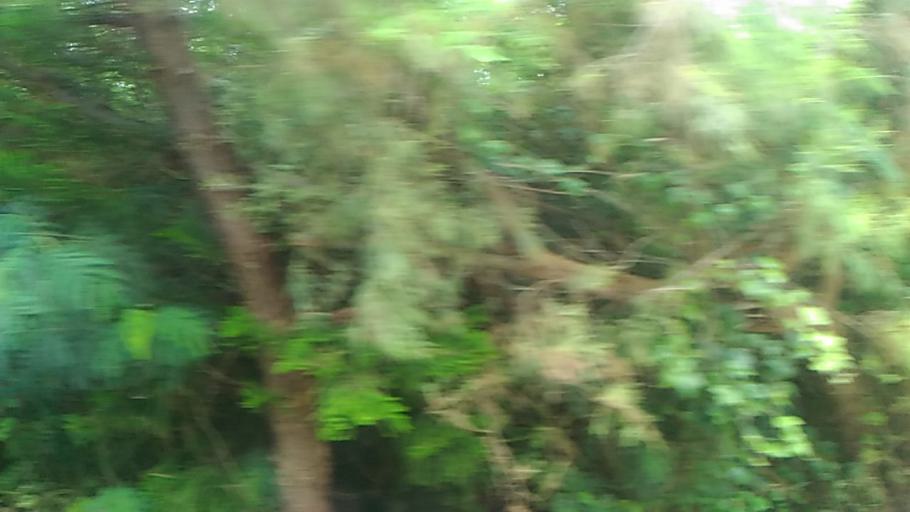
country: TW
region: Taiwan
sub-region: Penghu
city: Ma-kung
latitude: 23.3743
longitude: 119.4974
